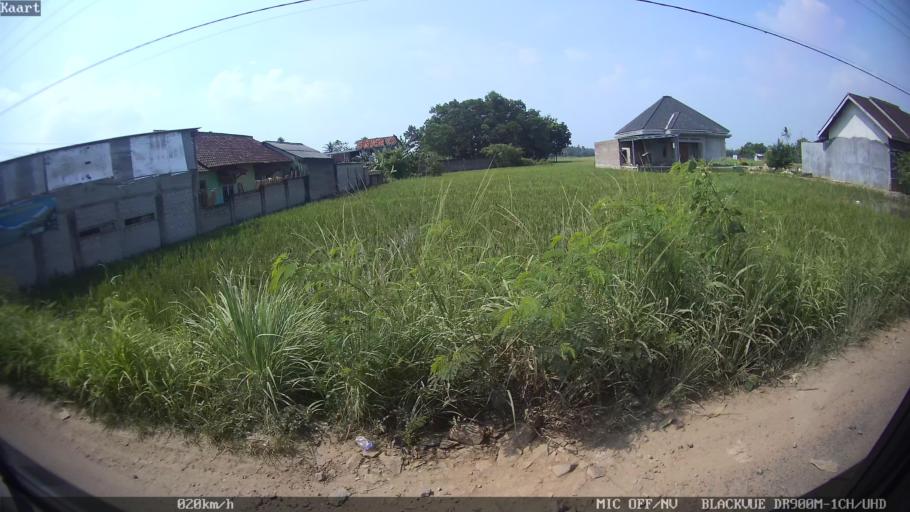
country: ID
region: Lampung
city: Natar
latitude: -5.3073
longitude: 105.2172
